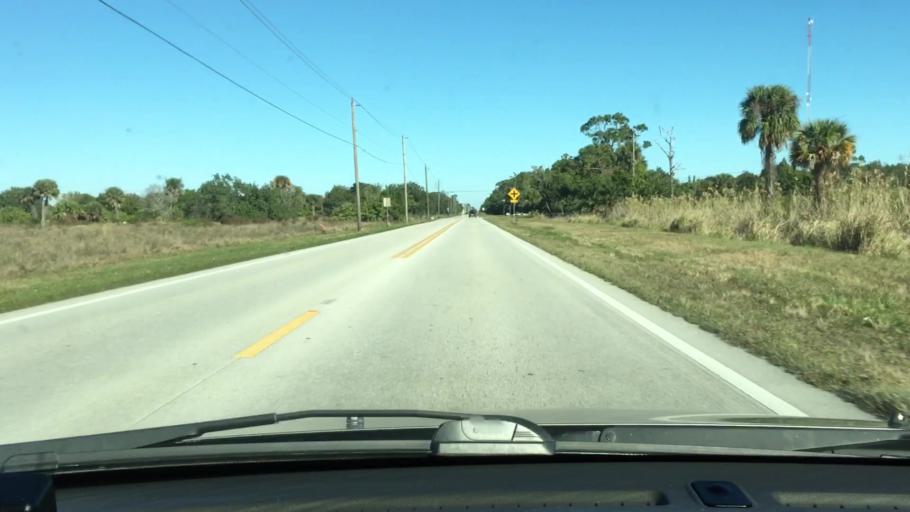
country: US
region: Florida
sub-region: Indian River County
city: Winter Beach
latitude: 27.7103
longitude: -80.4626
